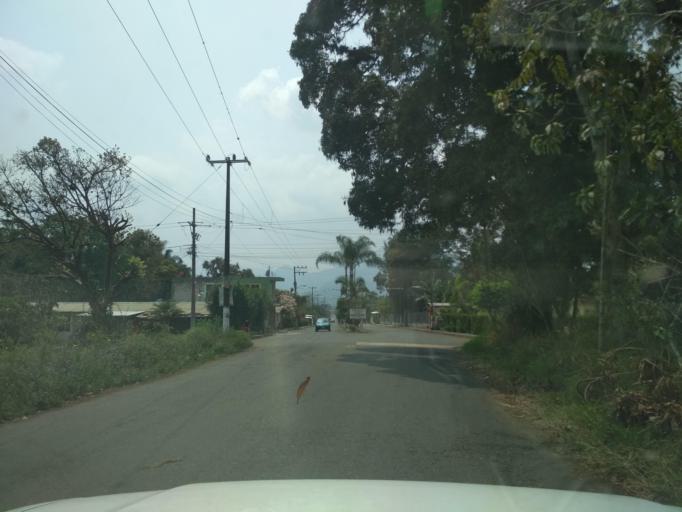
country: MX
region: Veracruz
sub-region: Cordoba
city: Fredepo
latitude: 18.8577
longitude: -96.9832
